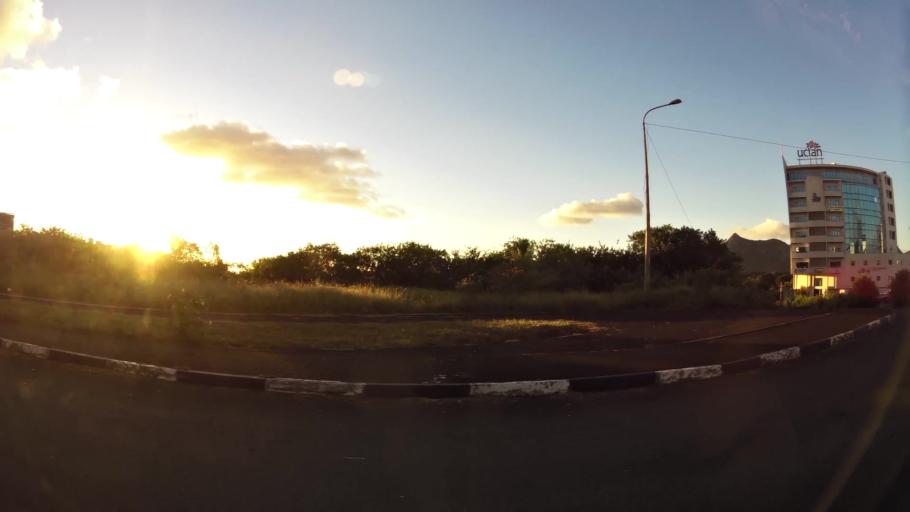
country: MU
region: Plaines Wilhems
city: Ebene
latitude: -20.2418
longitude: 57.4918
